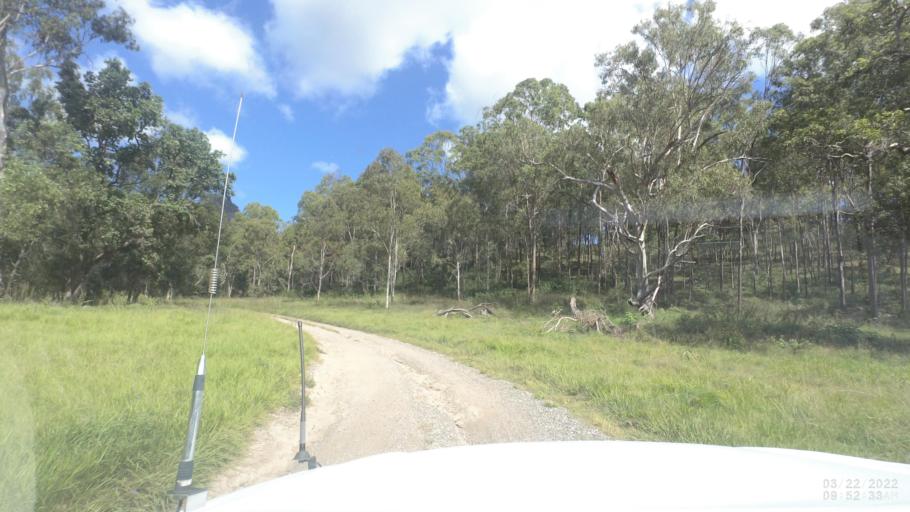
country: AU
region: Queensland
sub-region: Ipswich
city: Deebing Heights
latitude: -27.7524
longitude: 152.8105
